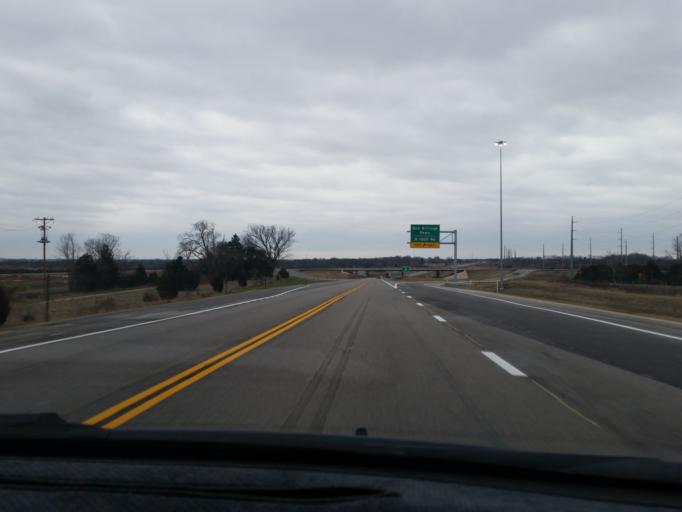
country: US
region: Kansas
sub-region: Douglas County
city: Lawrence
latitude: 38.9652
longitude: -95.3342
